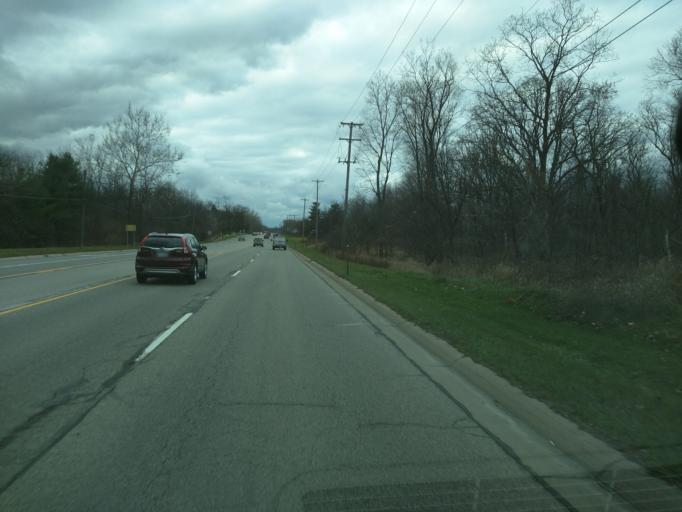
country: US
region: Michigan
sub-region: Ingham County
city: Haslett
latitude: 42.7152
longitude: -84.3949
